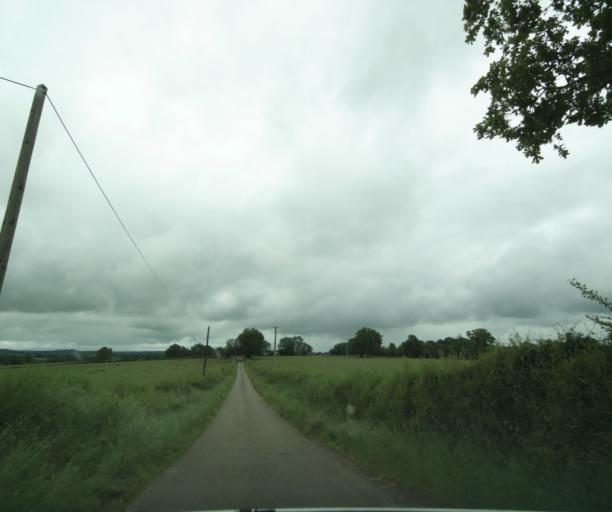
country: FR
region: Bourgogne
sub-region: Departement de Saone-et-Loire
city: Charolles
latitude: 46.4662
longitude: 4.3499
